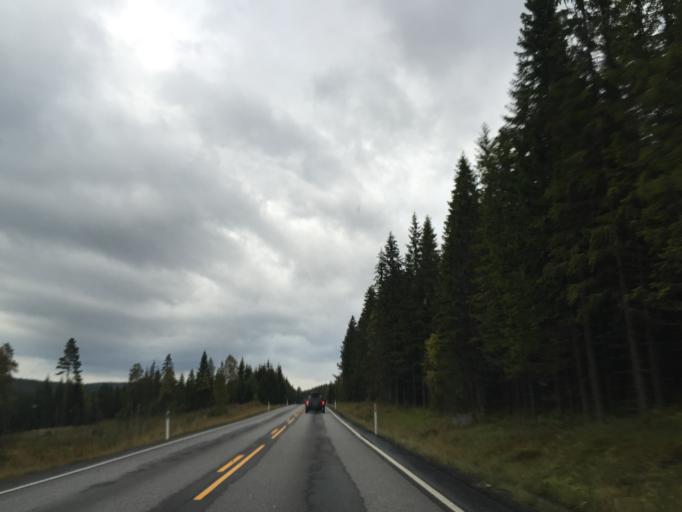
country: NO
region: Hedmark
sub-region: Nord-Odal
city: Sand
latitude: 60.4778
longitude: 11.5042
